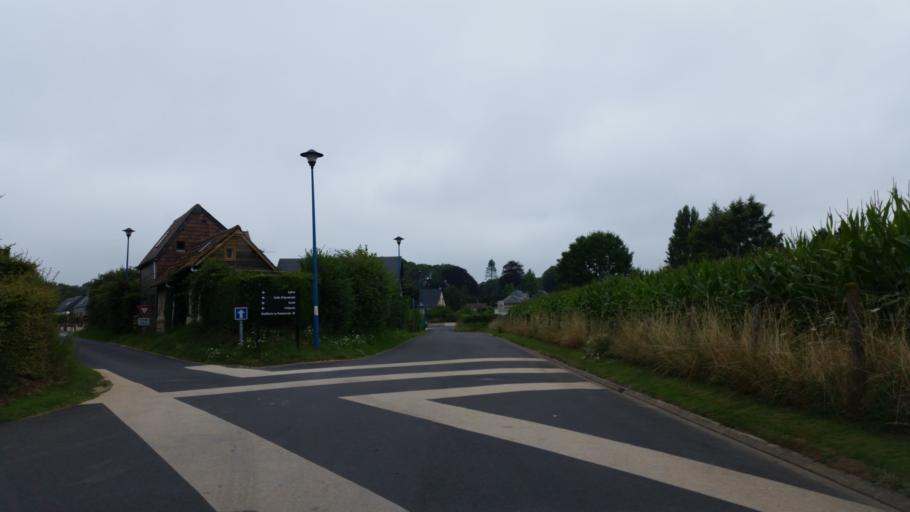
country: FR
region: Lower Normandy
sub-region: Departement du Calvados
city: La Riviere-Saint-Sauveur
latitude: 49.3834
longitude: 0.2445
